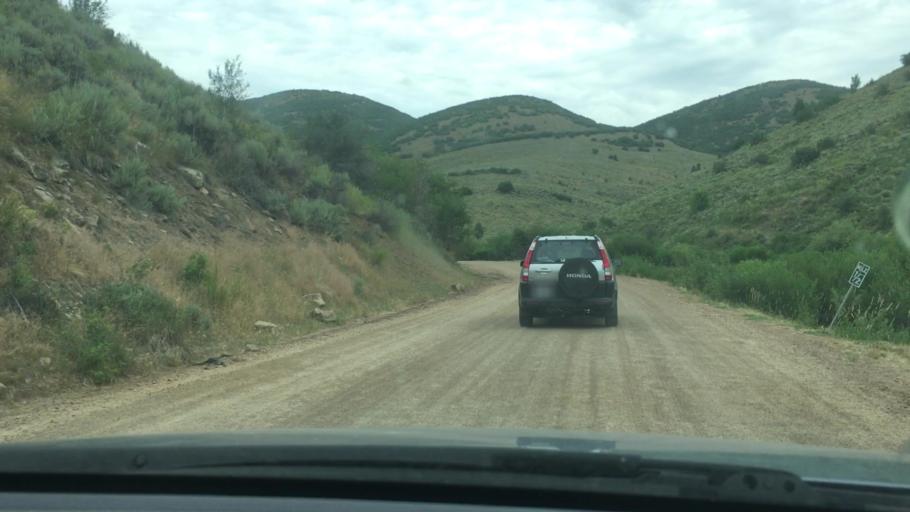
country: US
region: Utah
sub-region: Summit County
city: Summit Park
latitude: 40.7743
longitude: -111.5892
